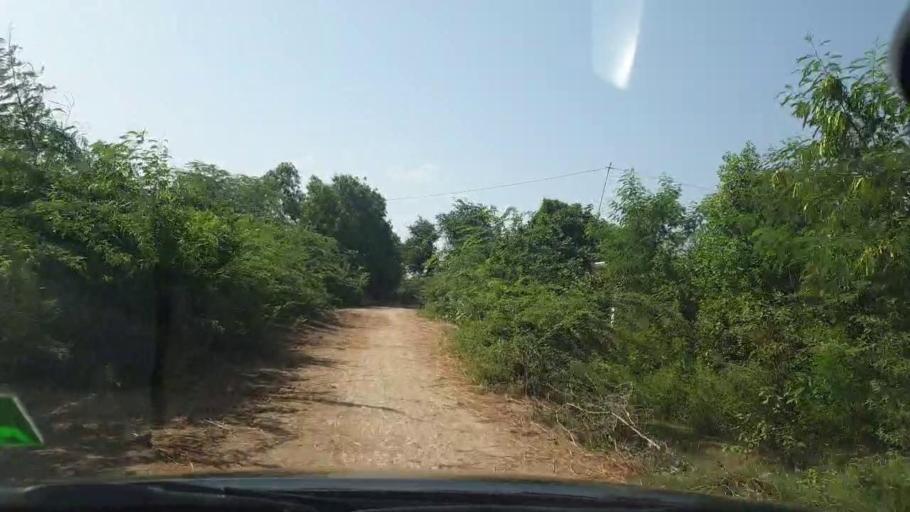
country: PK
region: Sindh
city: Tando Bago
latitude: 24.7698
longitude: 68.9450
